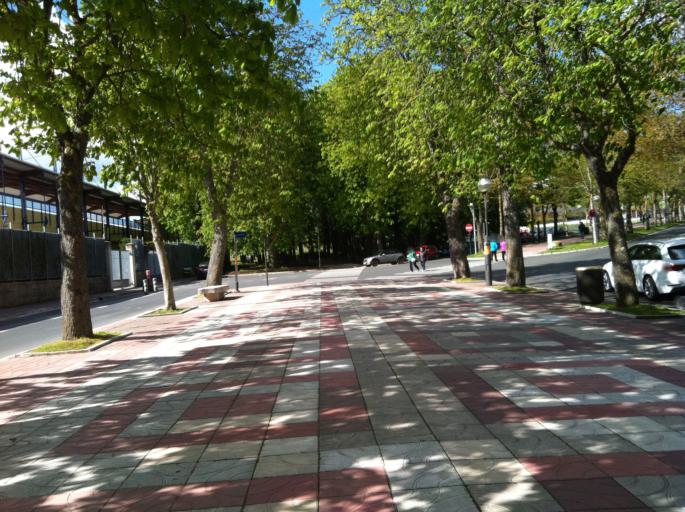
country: ES
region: Basque Country
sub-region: Provincia de Alava
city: Gasteiz / Vitoria
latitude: 42.8361
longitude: -2.6909
